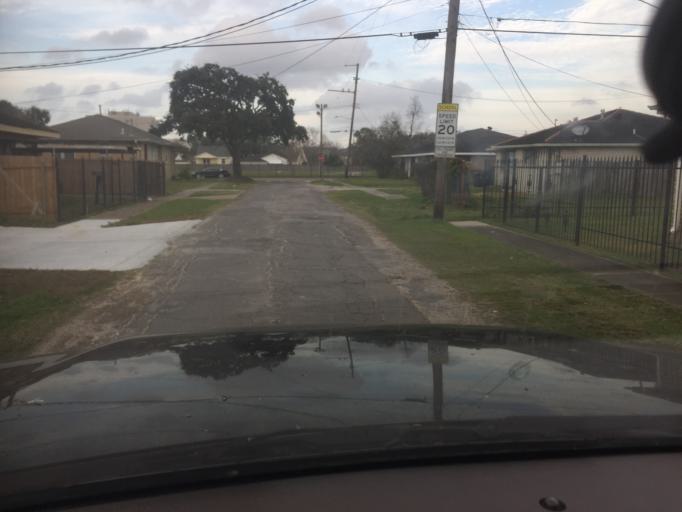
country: US
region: Louisiana
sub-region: Orleans Parish
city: New Orleans
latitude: 29.9871
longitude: -90.0829
